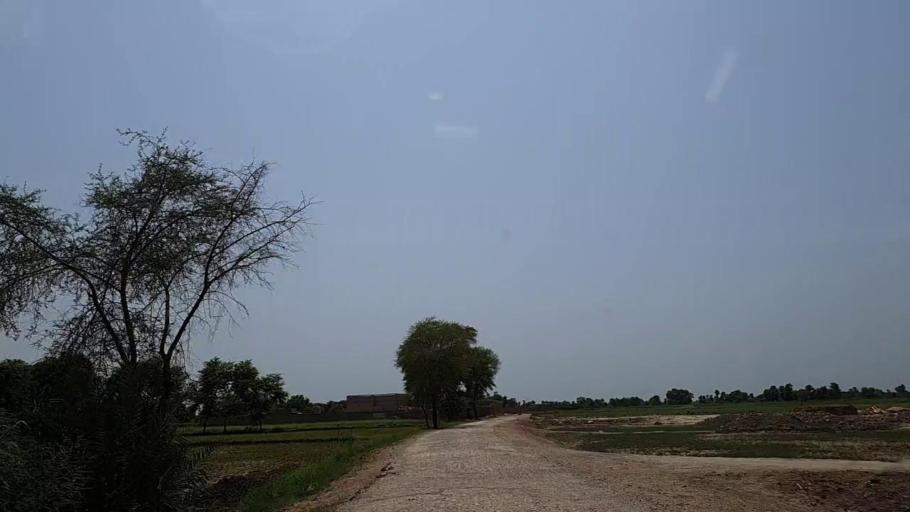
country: PK
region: Sindh
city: Adilpur
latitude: 27.9689
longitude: 69.3917
